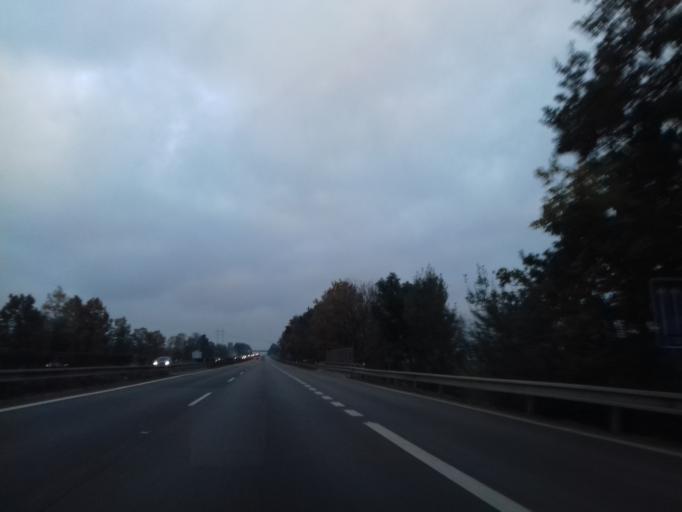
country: CZ
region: Central Bohemia
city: Cechtice
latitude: 49.6591
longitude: 15.1210
